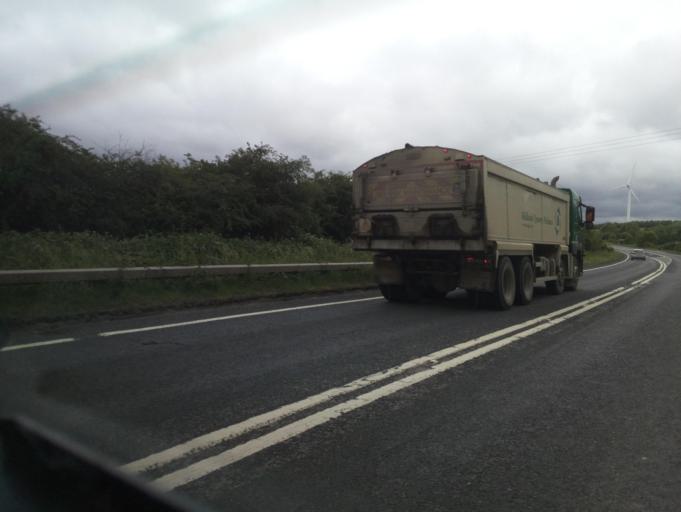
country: GB
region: England
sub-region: Leicestershire
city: Ashby de la Zouch
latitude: 52.7428
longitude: -1.4393
